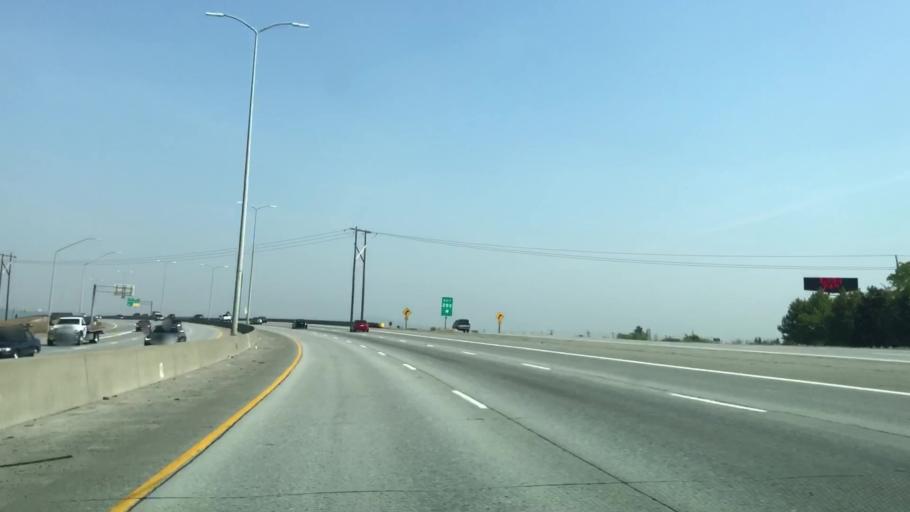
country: US
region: Washington
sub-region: Spokane County
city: Dishman
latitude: 47.6547
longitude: -117.3244
